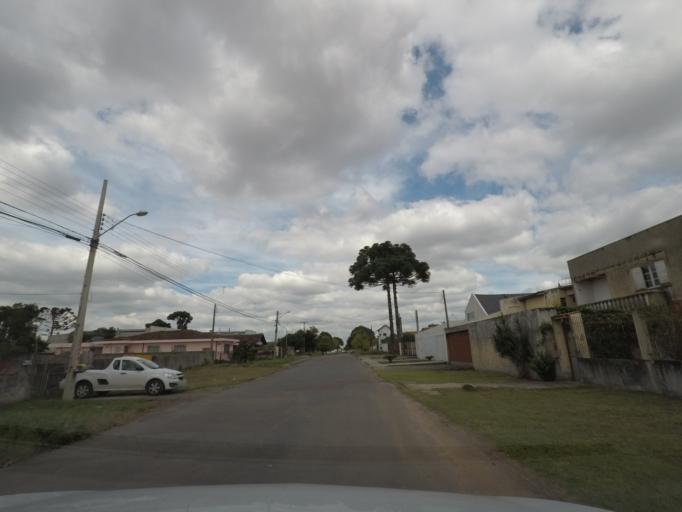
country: BR
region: Parana
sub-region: Sao Jose Dos Pinhais
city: Sao Jose dos Pinhais
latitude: -25.4921
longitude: -49.2367
